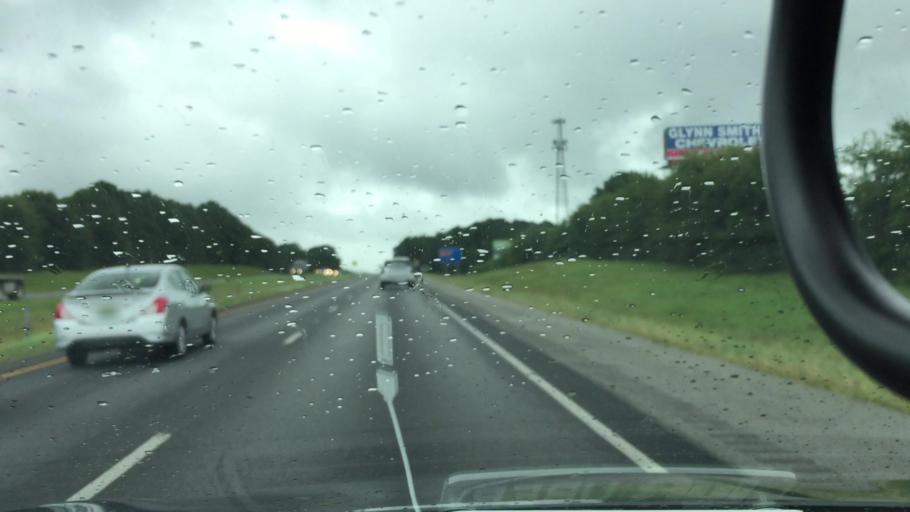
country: US
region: Alabama
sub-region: Lee County
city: Opelika
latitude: 32.6284
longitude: -85.3787
